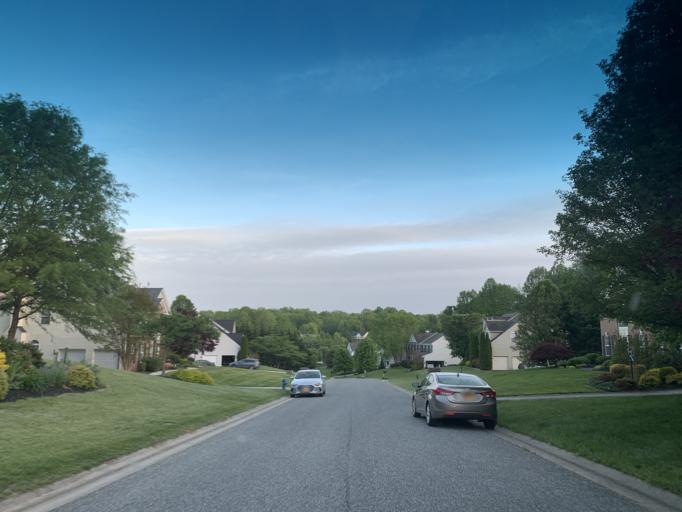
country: US
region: Maryland
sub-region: Harford County
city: South Bel Air
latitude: 39.5668
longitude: -76.2794
